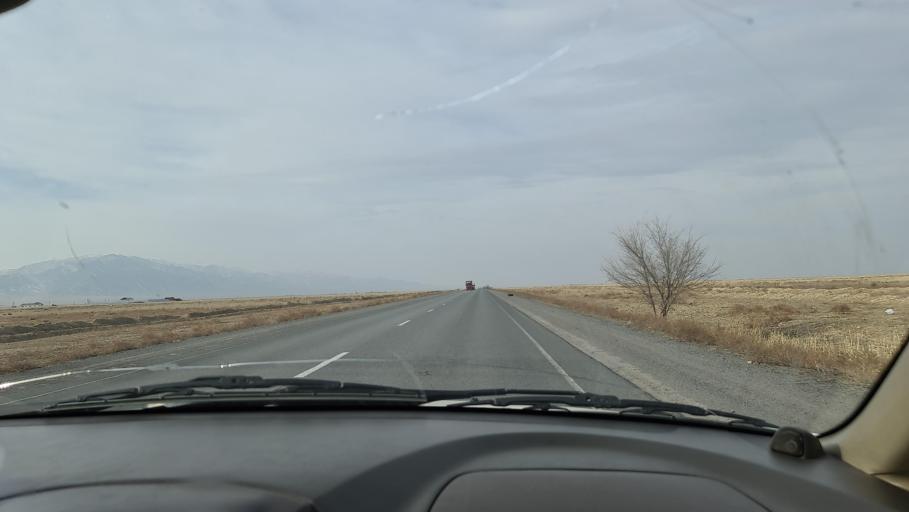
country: KG
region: Chuy
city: Bystrovka
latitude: 43.3360
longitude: 75.6020
